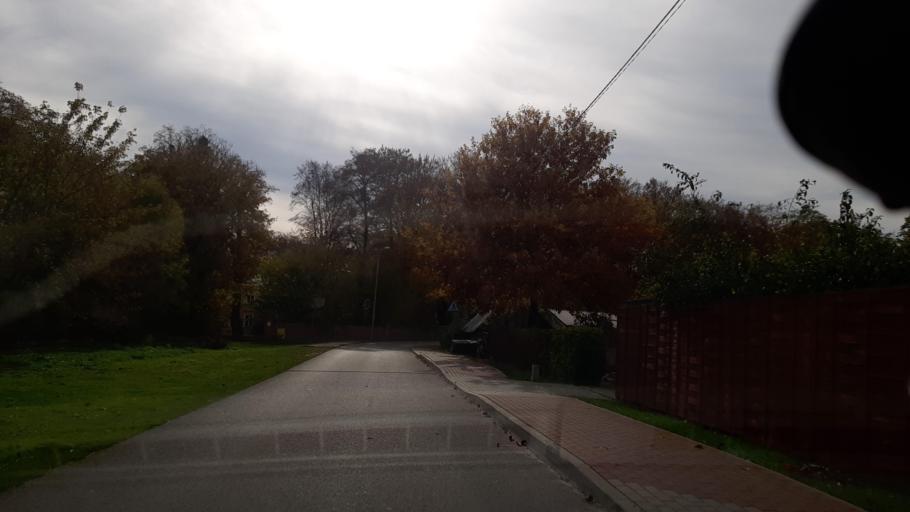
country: PL
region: Lublin Voivodeship
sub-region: Powiat pulawski
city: Markuszow
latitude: 51.3616
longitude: 22.2909
